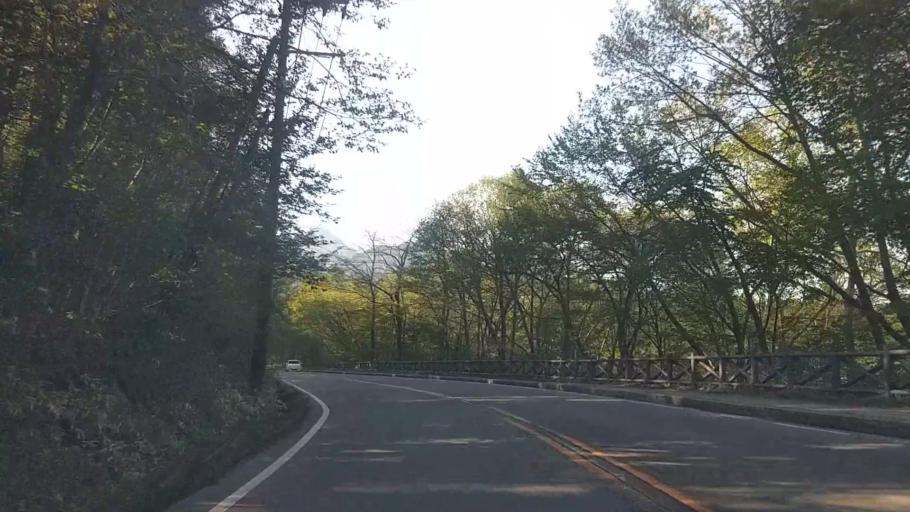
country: JP
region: Yamanashi
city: Nirasaki
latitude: 35.9200
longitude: 138.4063
